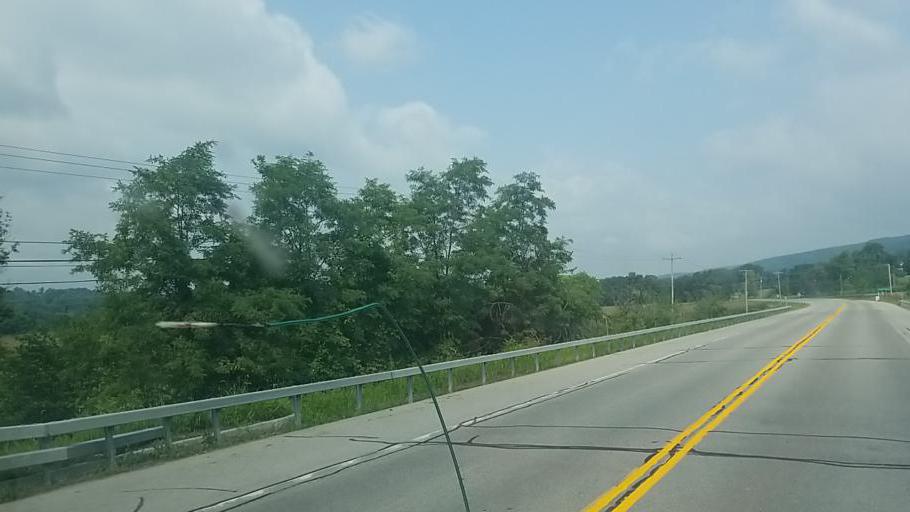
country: US
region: New York
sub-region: Montgomery County
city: Fort Plain
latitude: 42.9683
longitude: -74.6286
